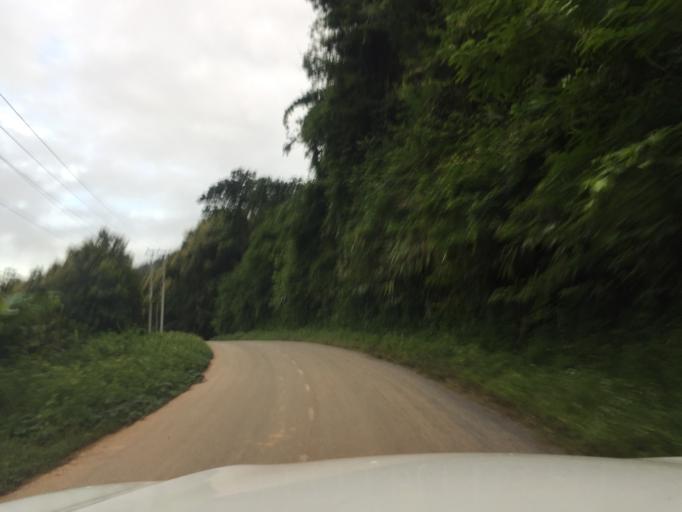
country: LA
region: Phongsali
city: Khoa
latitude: 21.0799
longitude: 102.3741
